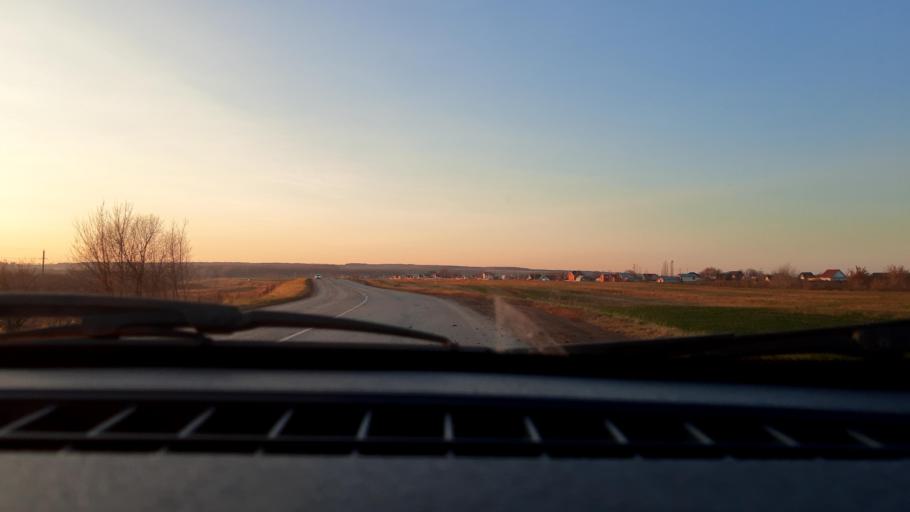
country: RU
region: Bashkortostan
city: Mikhaylovka
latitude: 54.8293
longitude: 55.9654
